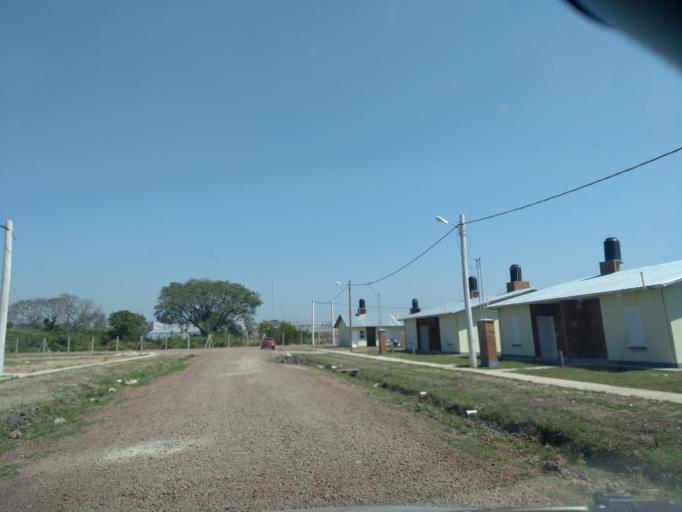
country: AR
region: Chaco
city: Fontana
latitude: -27.4073
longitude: -58.9743
